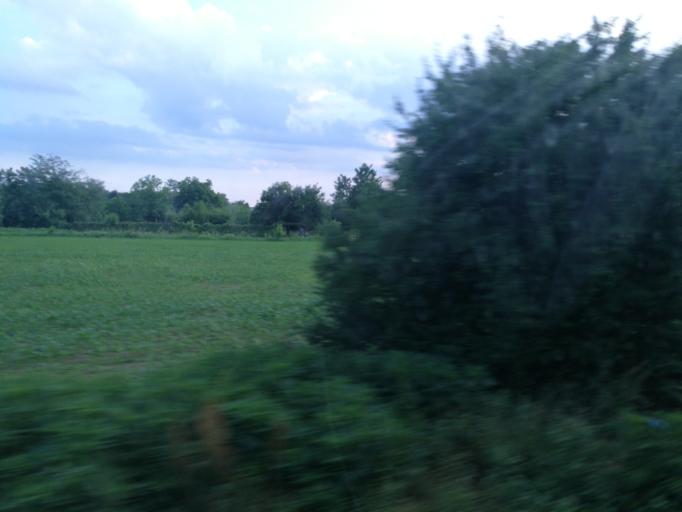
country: RO
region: Dambovita
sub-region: Comuna Titu
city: Titu
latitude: 44.6662
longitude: 25.5391
